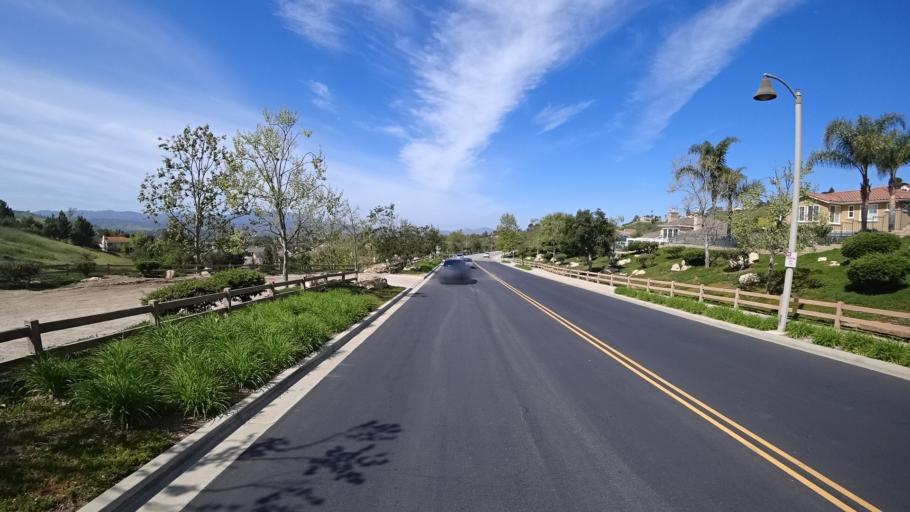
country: US
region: California
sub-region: Ventura County
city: Thousand Oaks
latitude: 34.2233
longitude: -118.8291
